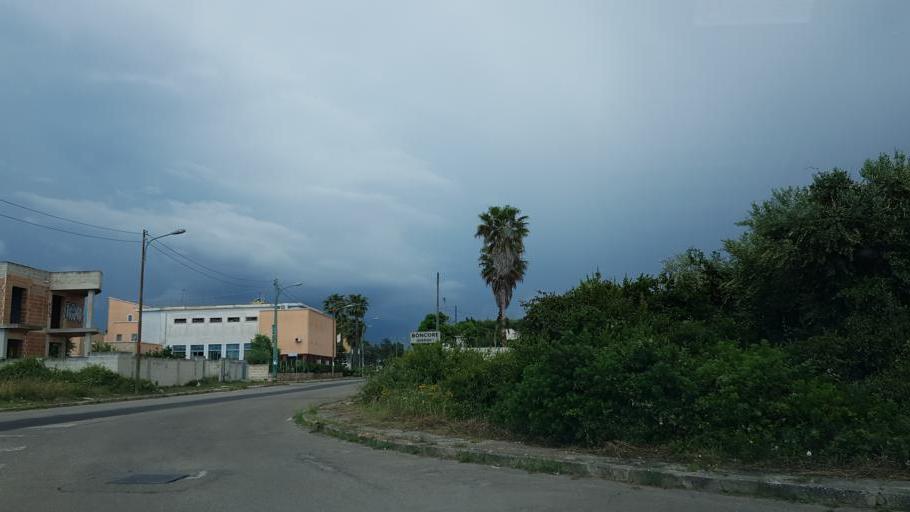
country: IT
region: Apulia
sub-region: Provincia di Lecce
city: Porto Cesareo
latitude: 40.2945
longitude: 17.8578
